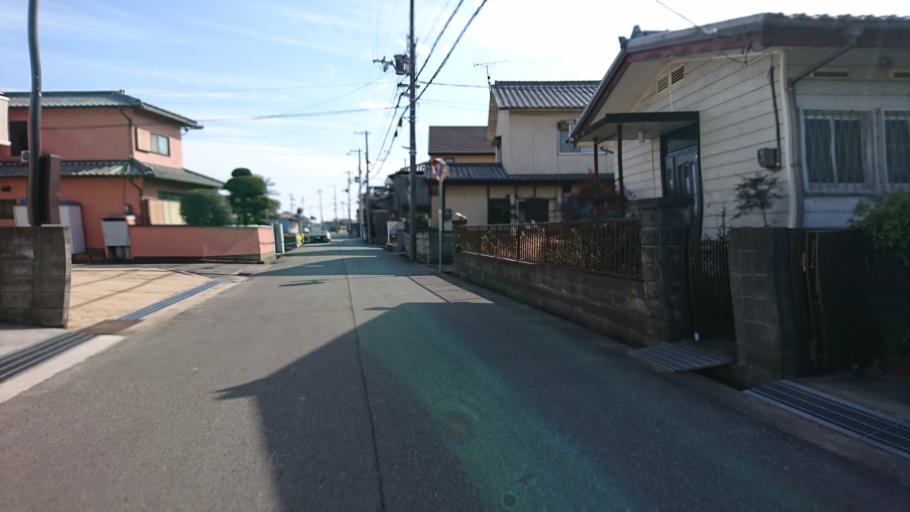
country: JP
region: Hyogo
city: Kakogawacho-honmachi
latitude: 34.7856
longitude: 134.8342
